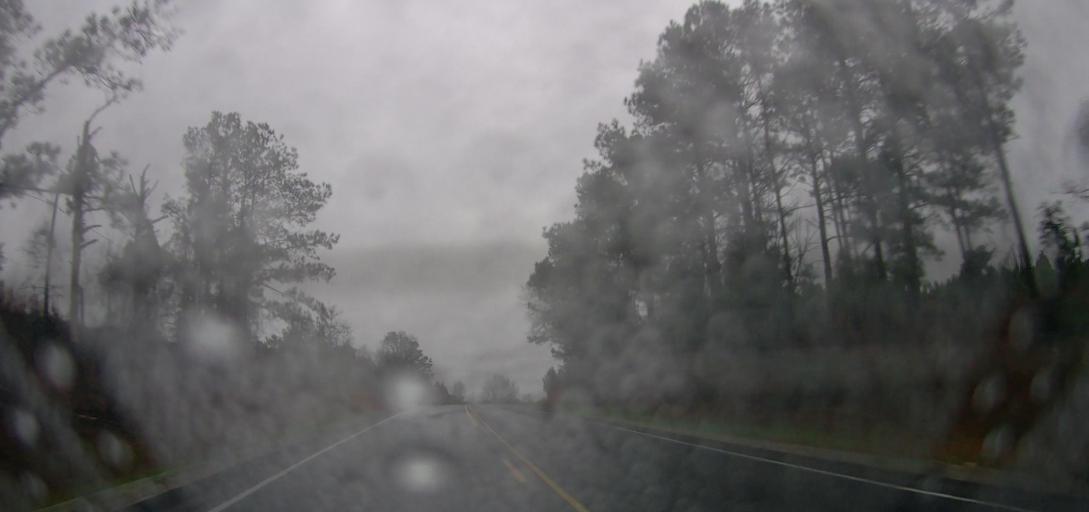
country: US
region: Alabama
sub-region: Chilton County
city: Clanton
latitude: 32.6410
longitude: -86.7540
